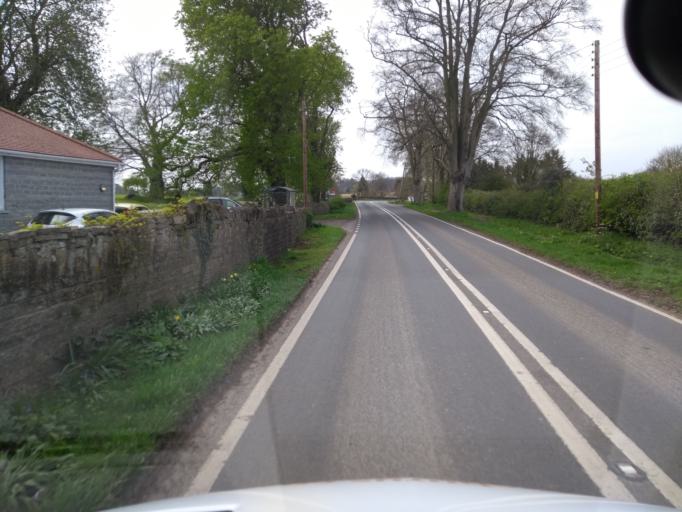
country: GB
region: England
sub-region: Somerset
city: Langport
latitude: 51.0345
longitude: -2.8424
